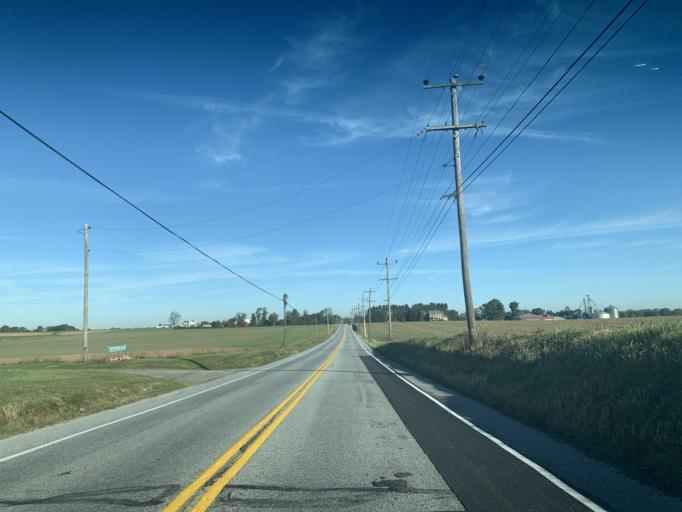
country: US
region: Pennsylvania
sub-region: Chester County
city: Parkesburg
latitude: 39.8782
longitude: -75.9215
